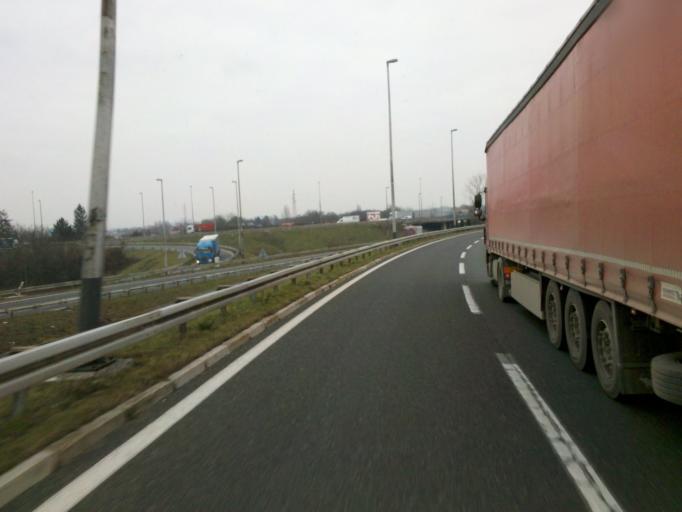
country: HR
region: Grad Zagreb
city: Lucko
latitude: 45.7572
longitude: 15.8978
